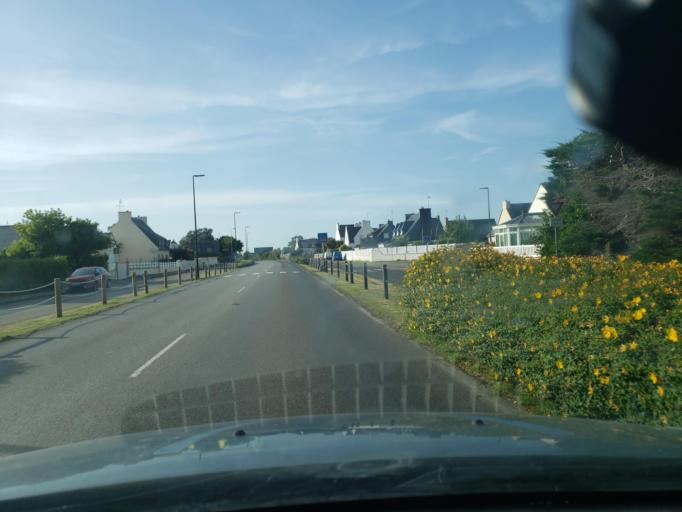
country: FR
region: Brittany
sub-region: Departement du Finistere
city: Guilvinec
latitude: 47.8056
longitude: -4.2791
